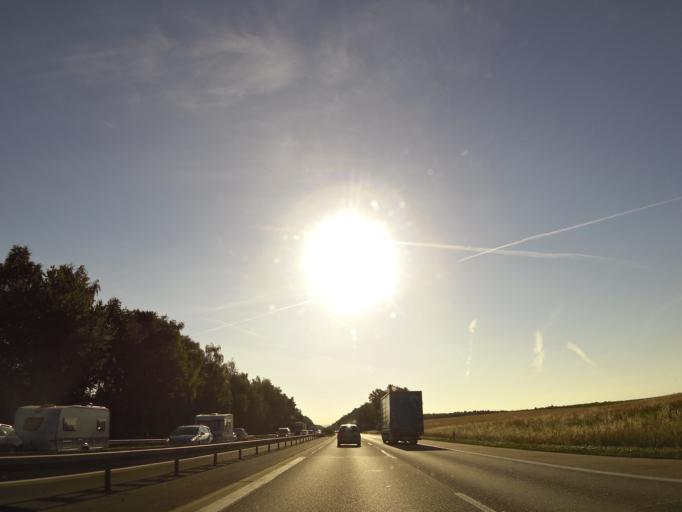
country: DE
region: Bavaria
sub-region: Regierungsbezirk Mittelfranken
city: Wachenroth
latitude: 49.7322
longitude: 10.7339
